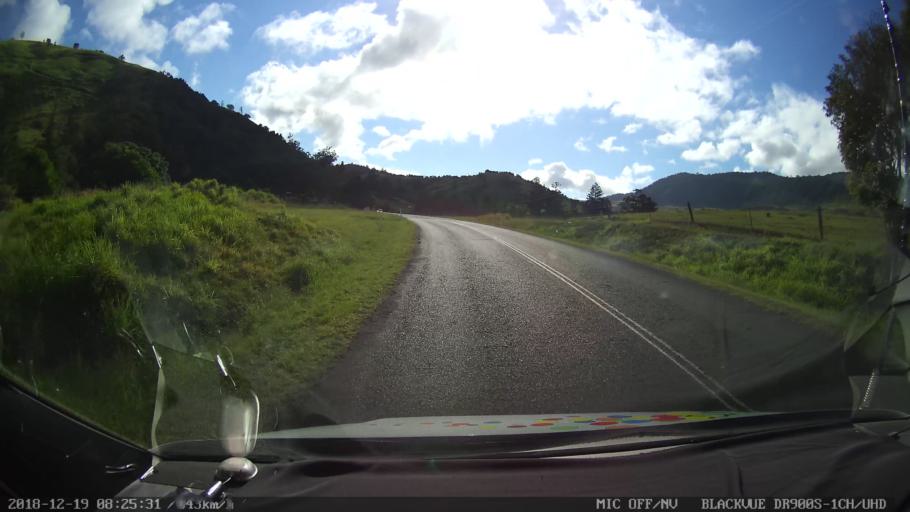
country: AU
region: New South Wales
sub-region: Kyogle
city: Kyogle
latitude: -28.3147
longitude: 152.9169
